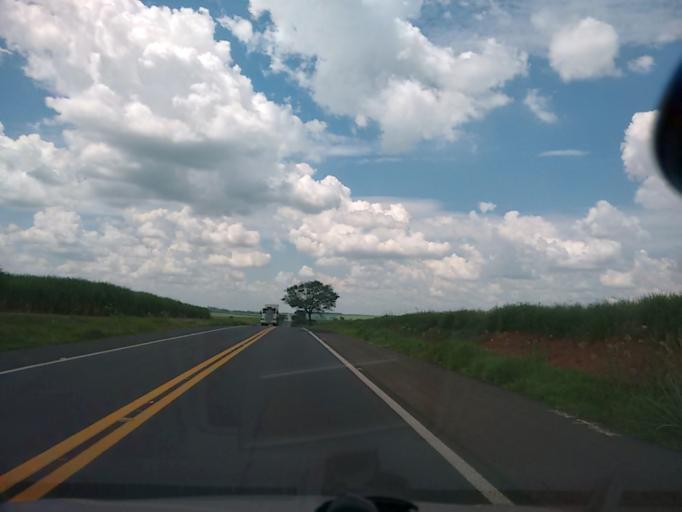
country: BR
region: Sao Paulo
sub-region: Osvaldo Cruz
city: Osvaldo Cruz
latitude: -21.9021
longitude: -50.8834
